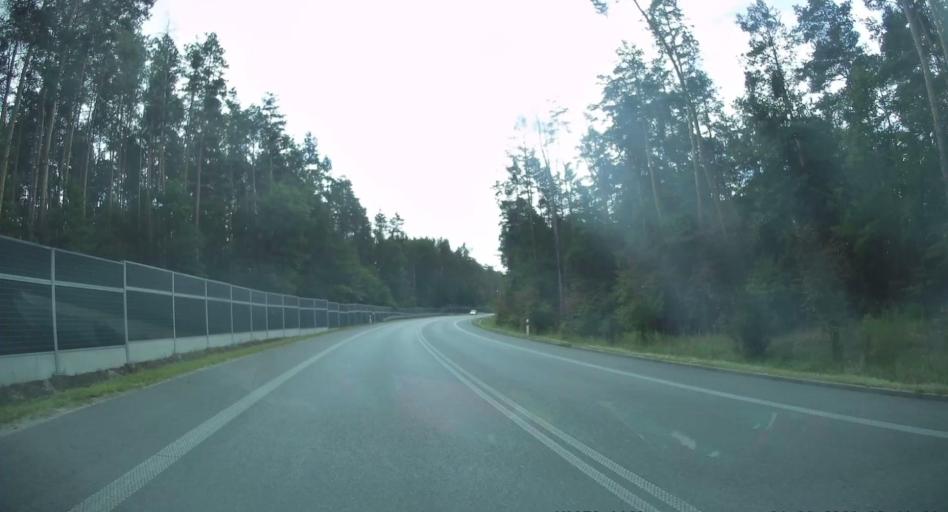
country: PL
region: Subcarpathian Voivodeship
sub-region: Powiat mielecki
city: Mielec
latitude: 50.2831
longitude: 21.4987
